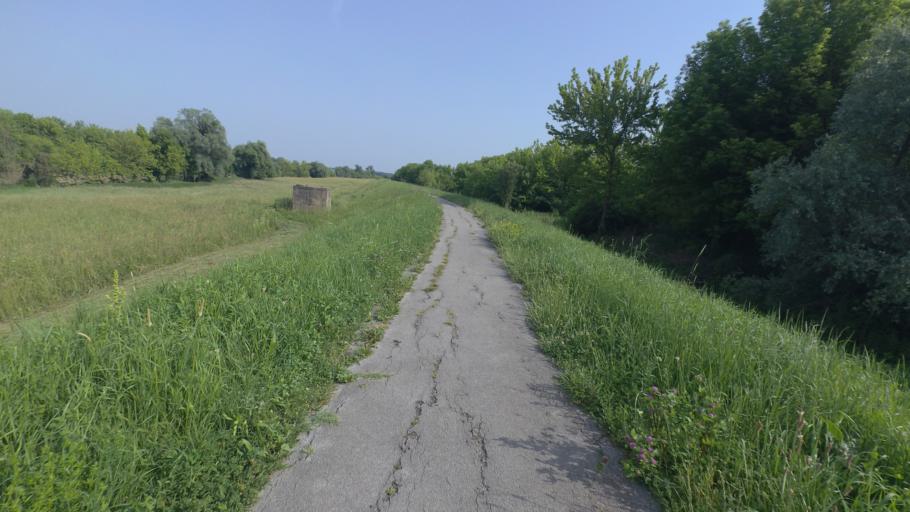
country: HR
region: Karlovacka
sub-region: Grad Karlovac
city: Karlovac
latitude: 45.4986
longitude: 15.5667
